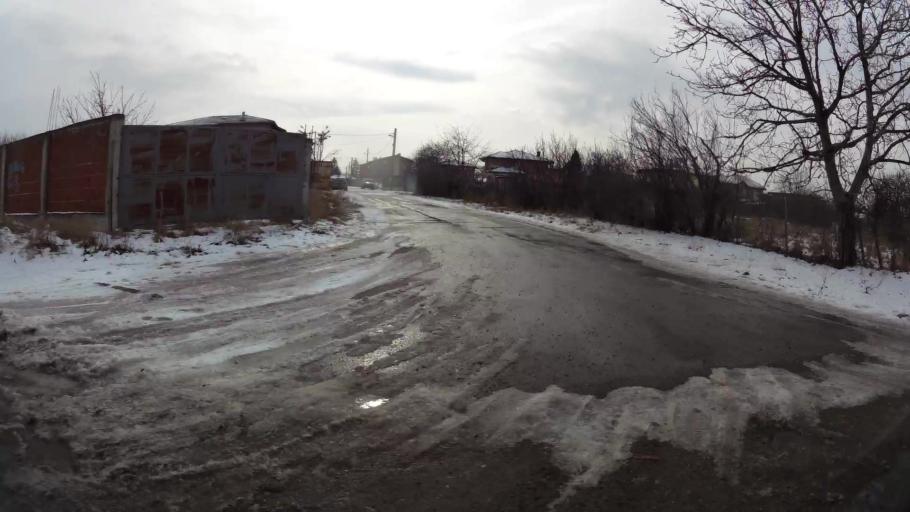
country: BG
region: Sofia-Capital
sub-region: Stolichna Obshtina
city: Sofia
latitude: 42.7170
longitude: 23.4064
